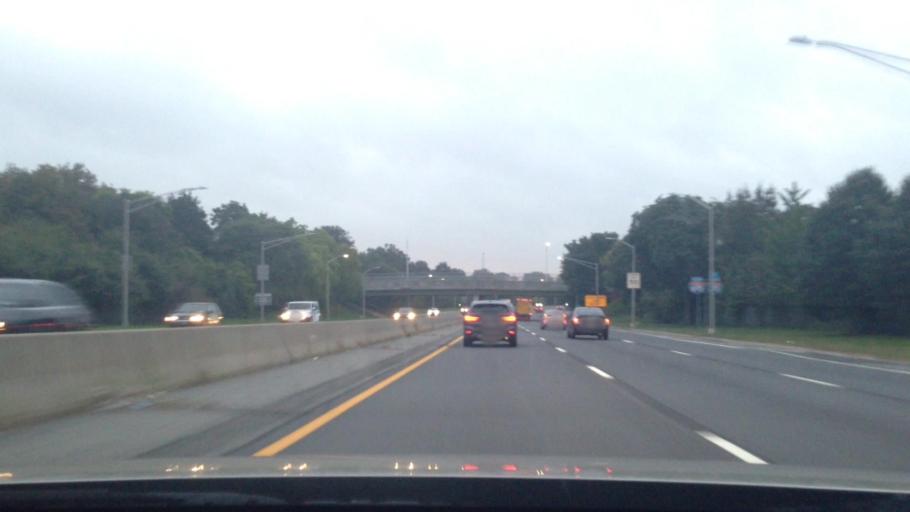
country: US
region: New York
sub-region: Bronx
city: The Bronx
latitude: 40.8294
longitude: -73.8190
